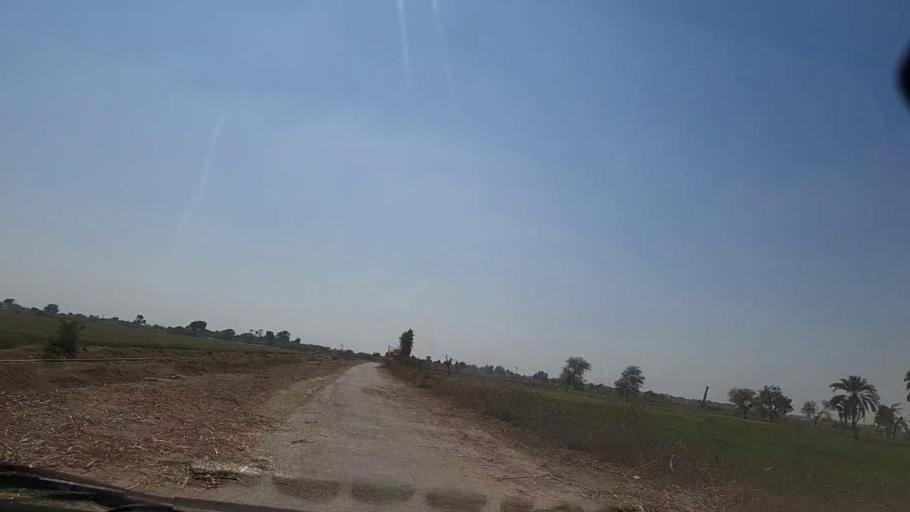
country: PK
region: Sindh
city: Mirwah Gorchani
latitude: 25.3701
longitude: 68.9928
